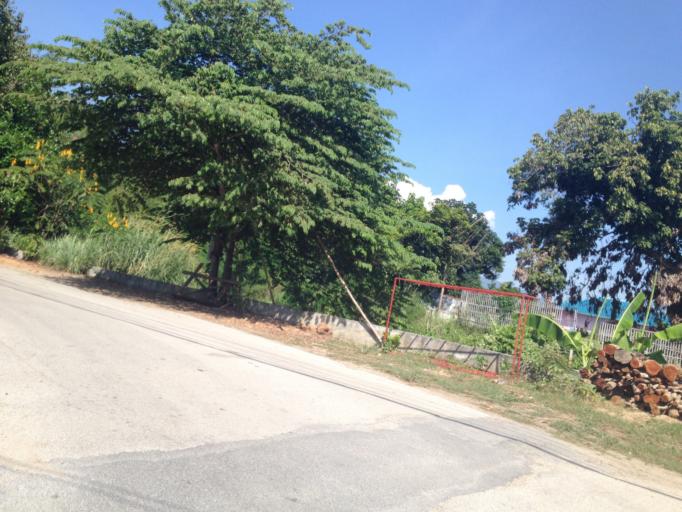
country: TH
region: Chiang Mai
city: Hang Dong
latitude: 18.7102
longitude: 98.9133
